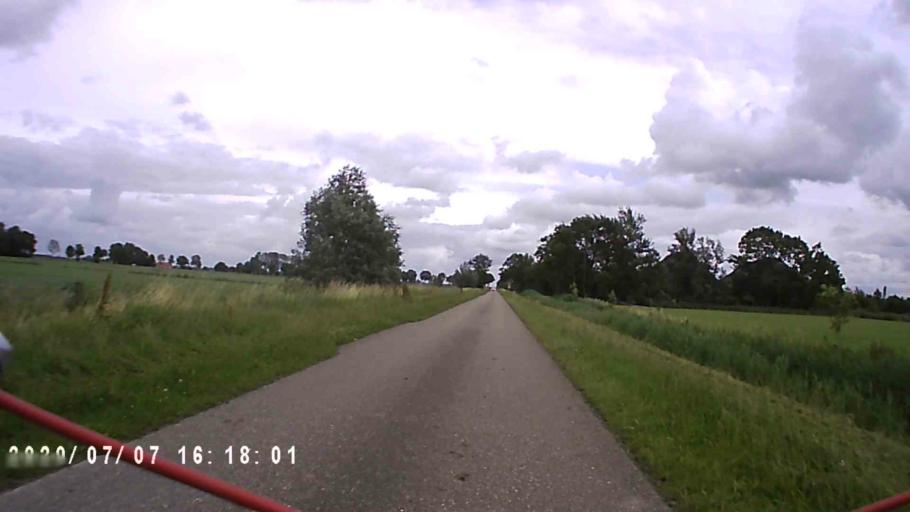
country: NL
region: Groningen
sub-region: Gemeente Winsum
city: Winsum
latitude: 53.3706
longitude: 6.5653
